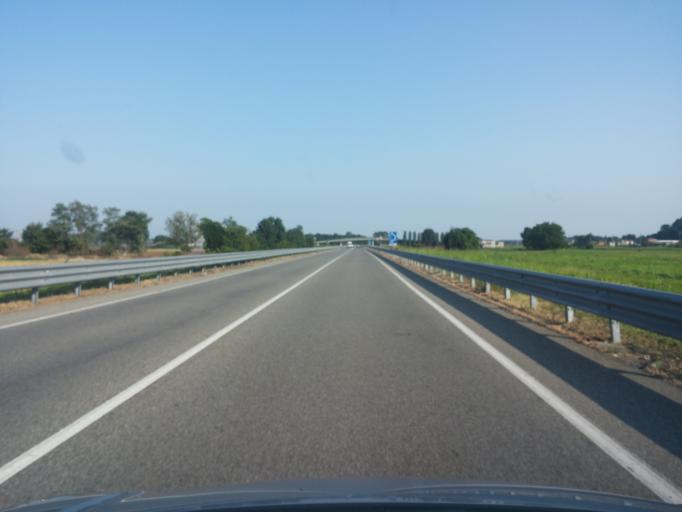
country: IT
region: Piedmont
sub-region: Provincia di Biella
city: Castelletto Cervo
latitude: 45.5227
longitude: 8.2024
